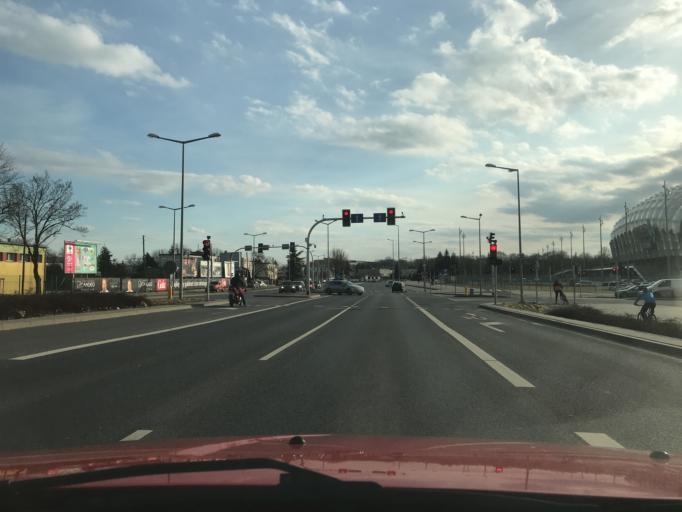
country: PL
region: Greater Poland Voivodeship
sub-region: Powiat poznanski
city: Lubon
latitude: 52.3991
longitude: 16.8630
